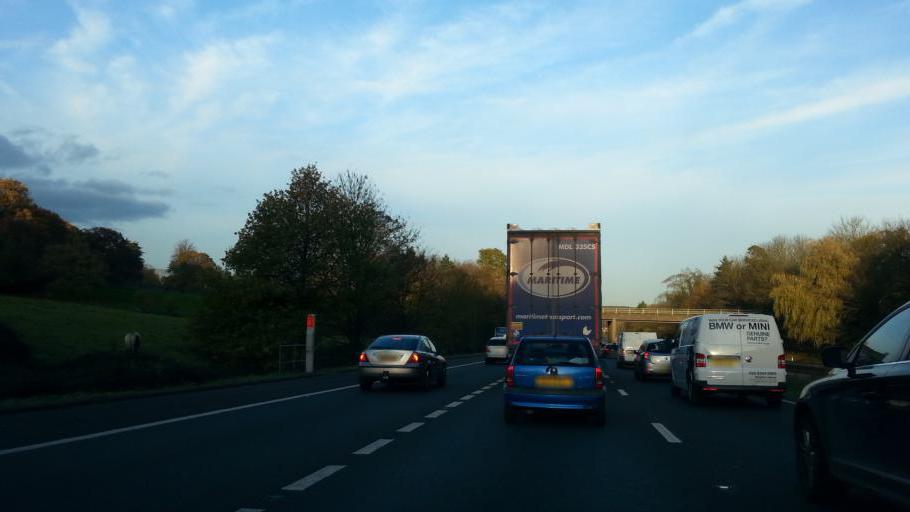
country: GB
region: England
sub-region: Hertfordshire
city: Welwyn
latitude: 51.8174
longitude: -0.2213
